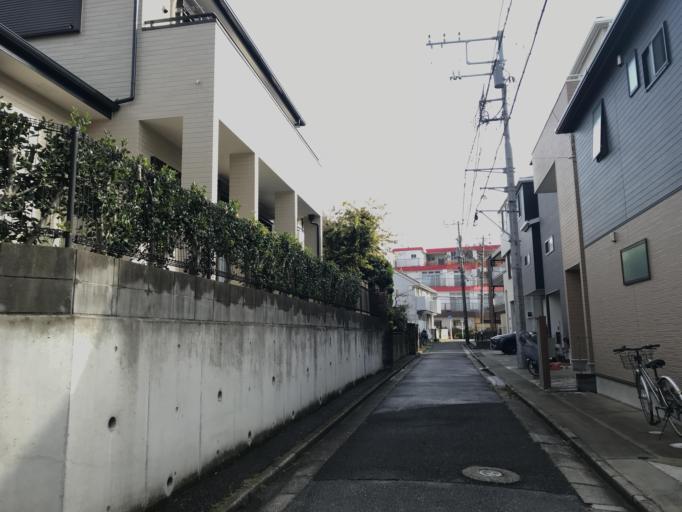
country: JP
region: Chiba
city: Funabashi
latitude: 35.6931
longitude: 139.9937
